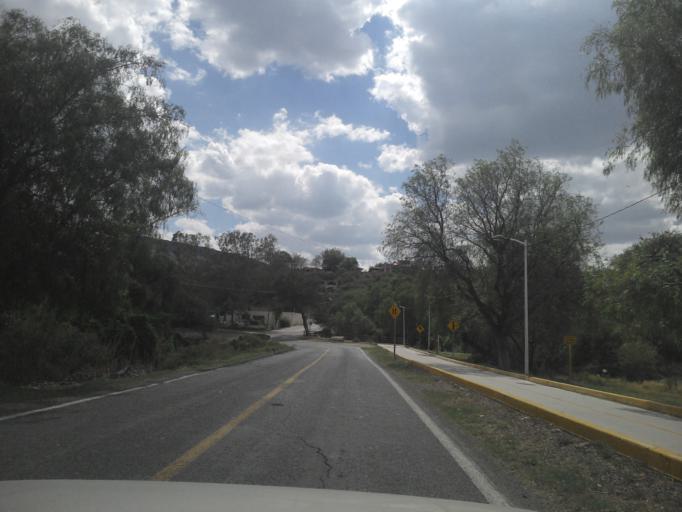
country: MX
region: Guanajuato
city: San Francisco del Rincon
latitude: 21.0311
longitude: -101.8866
